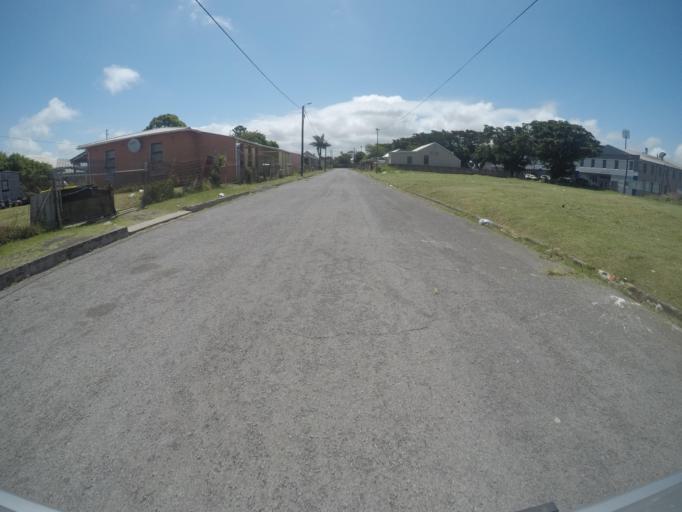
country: ZA
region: Eastern Cape
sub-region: Buffalo City Metropolitan Municipality
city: East London
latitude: -33.0103
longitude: 27.9051
